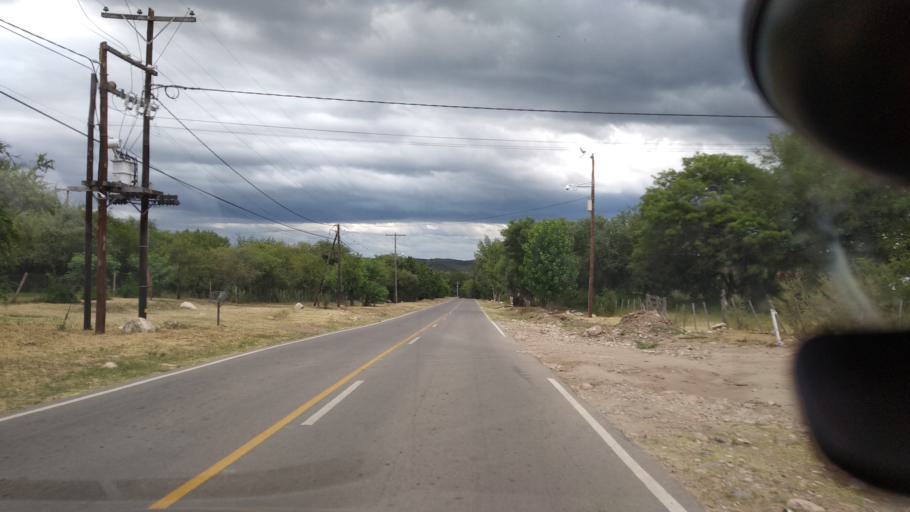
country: AR
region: Cordoba
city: Villa Las Rosas
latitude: -31.9381
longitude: -65.0377
